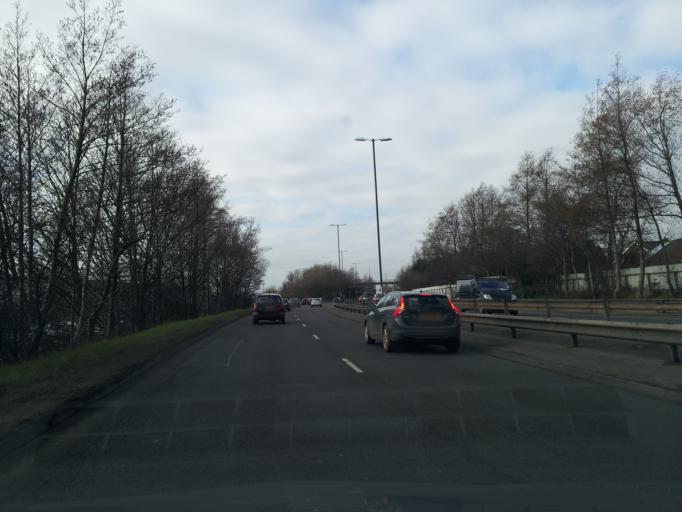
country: GB
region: England
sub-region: Derby
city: Derby
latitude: 52.9196
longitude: -1.4430
